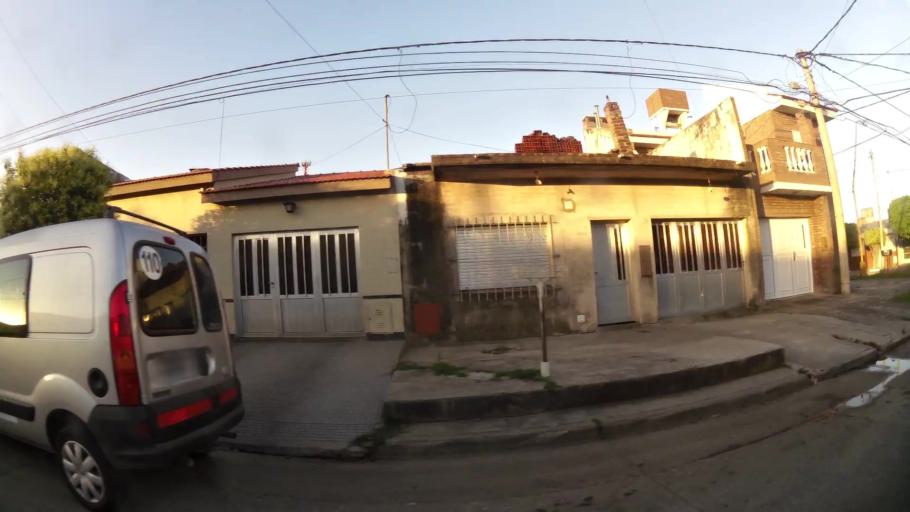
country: AR
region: Santa Fe
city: Santa Fe de la Vera Cruz
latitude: -31.6041
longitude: -60.6827
